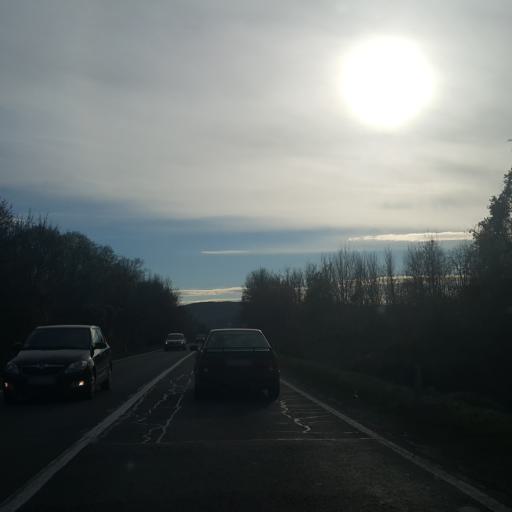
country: RS
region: Central Serbia
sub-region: Belgrade
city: Lazarevac
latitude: 44.3886
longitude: 20.2381
